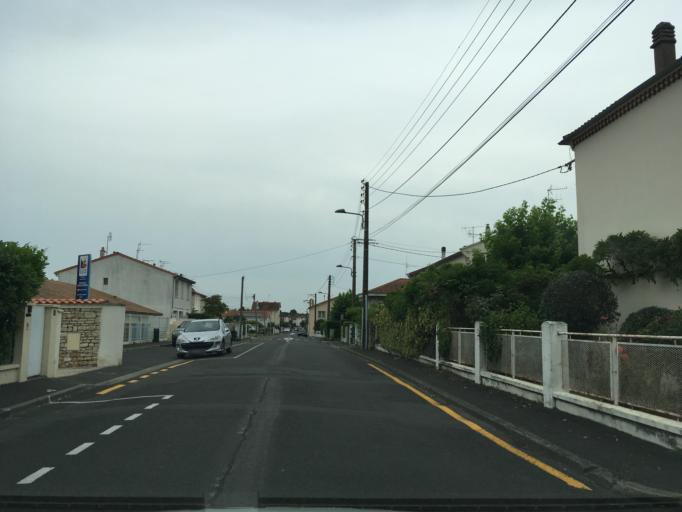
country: FR
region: Poitou-Charentes
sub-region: Departement des Deux-Sevres
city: Niort
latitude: 46.3279
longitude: -0.4736
